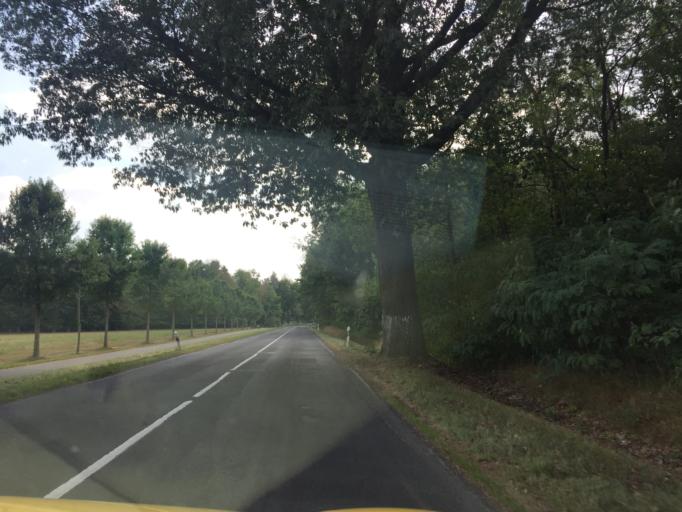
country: DE
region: Brandenburg
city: Welzow
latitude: 51.5636
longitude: 14.1781
